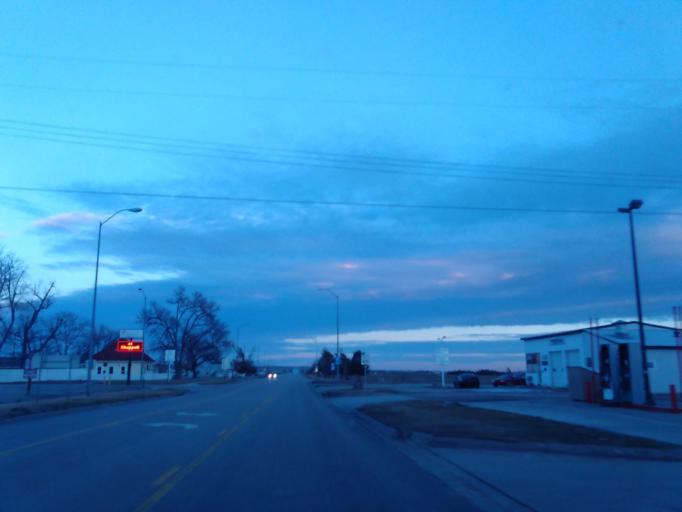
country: US
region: Nebraska
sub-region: Garden County
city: Oshkosh
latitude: 41.4022
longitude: -102.3467
